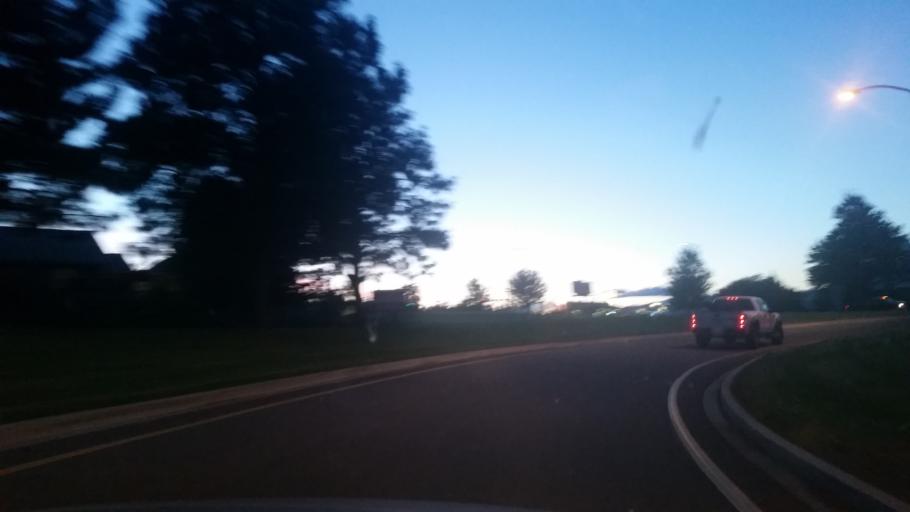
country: US
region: Washington
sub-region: Douglas County
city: East Wenatchee
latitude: 47.4087
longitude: -120.3012
